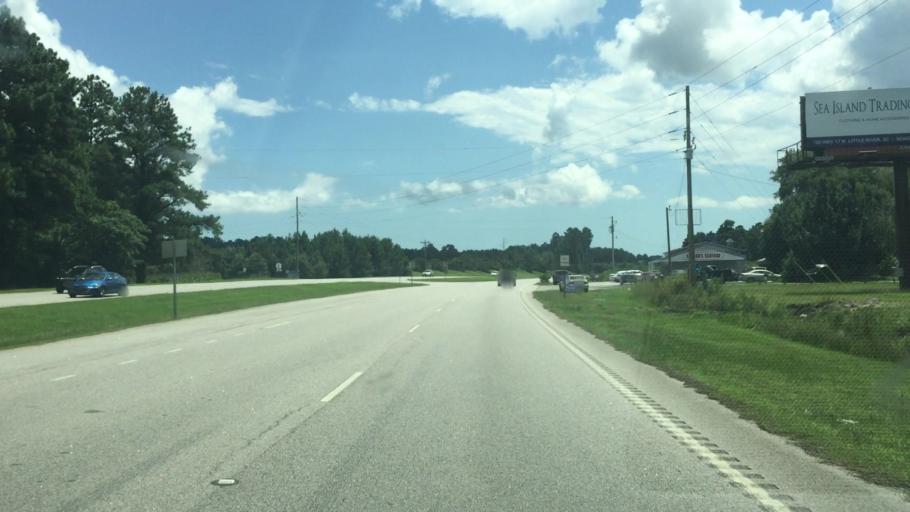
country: US
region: South Carolina
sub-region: Horry County
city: Little River
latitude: 33.9556
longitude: -78.7360
